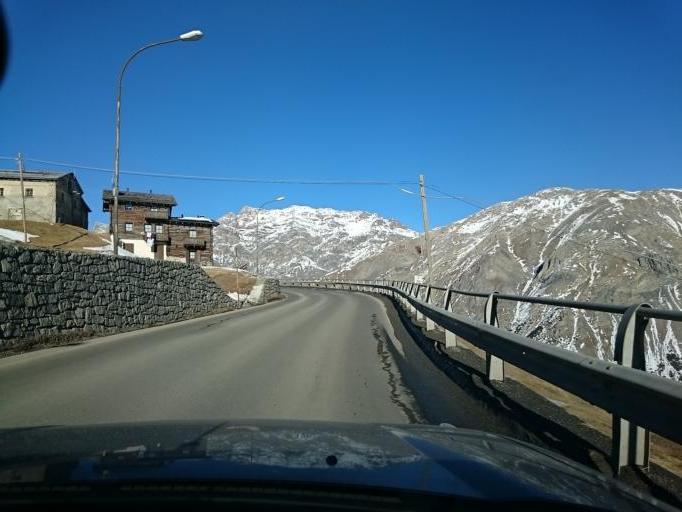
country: IT
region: Lombardy
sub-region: Provincia di Sondrio
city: Livigno
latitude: 46.5324
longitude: 10.1710
